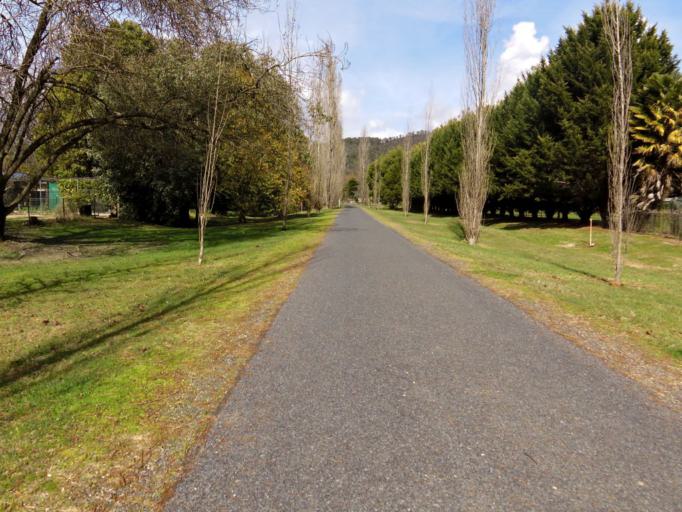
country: AU
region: Victoria
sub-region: Alpine
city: Mount Beauty
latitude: -36.7219
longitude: 146.9457
